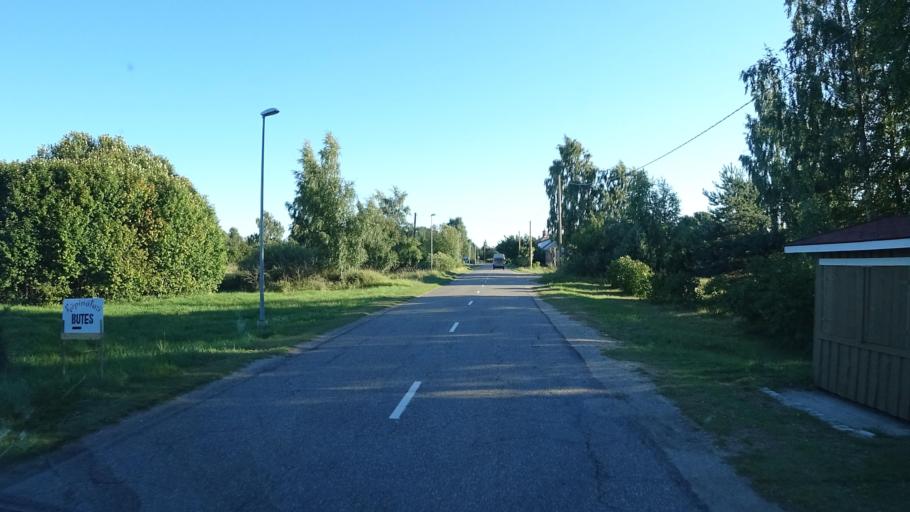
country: LV
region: Rojas
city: Roja
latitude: 57.7503
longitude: 22.5947
